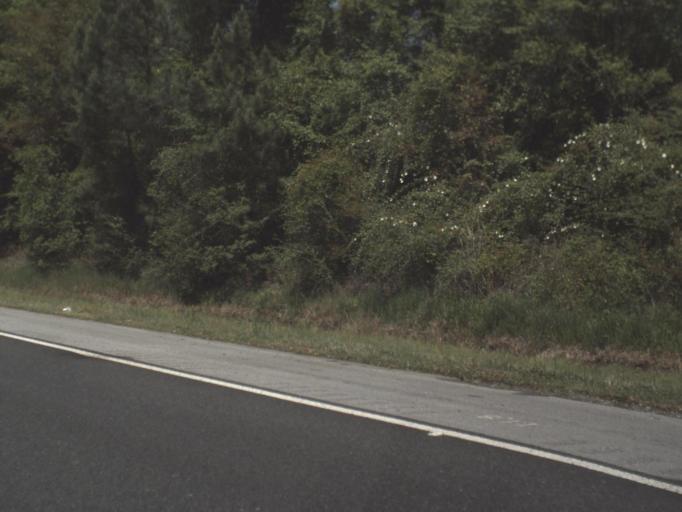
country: US
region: Florida
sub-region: Escambia County
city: Ferry Pass
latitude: 30.5038
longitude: -87.2405
